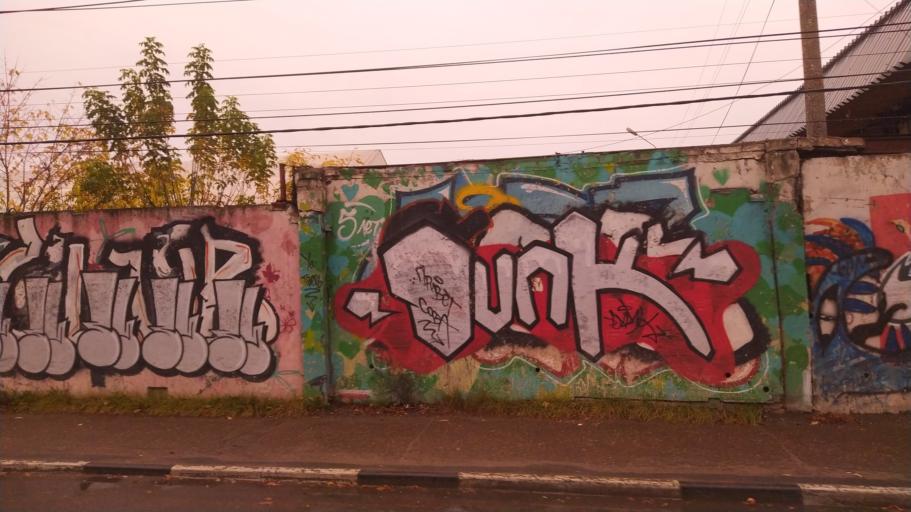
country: RU
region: Tverskaya
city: Tver
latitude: 56.8350
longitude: 35.9056
